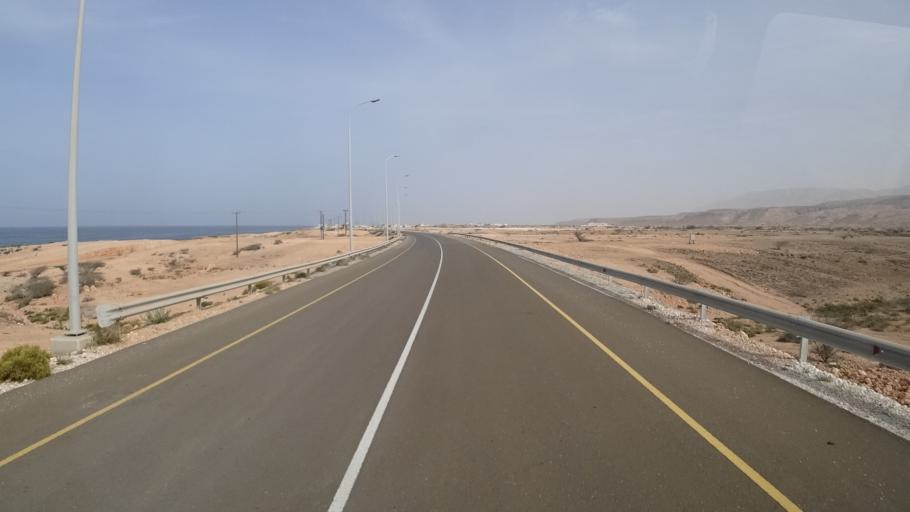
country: OM
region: Ash Sharqiyah
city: Sur
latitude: 23.0002
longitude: 59.1192
